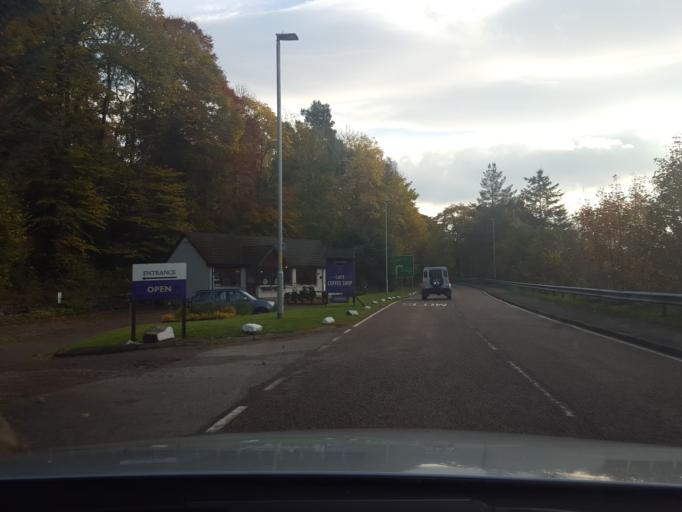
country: GB
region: Scotland
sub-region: Highland
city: Beauly
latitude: 57.2158
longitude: -4.6212
